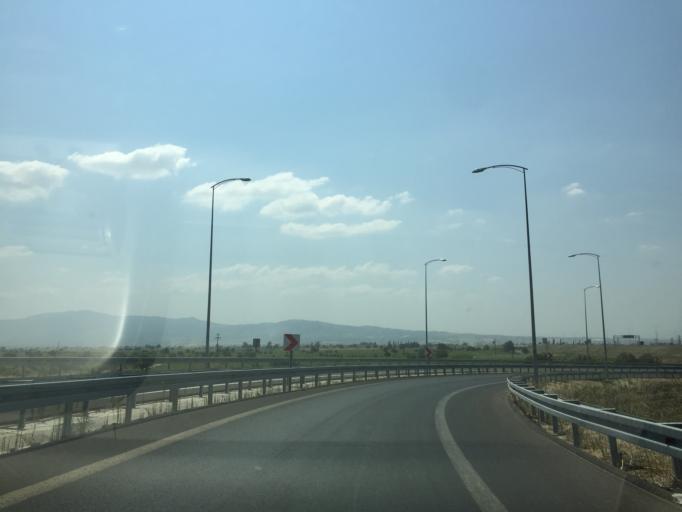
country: TR
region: Manisa
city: Halitpasa
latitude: 38.7663
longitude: 27.6624
